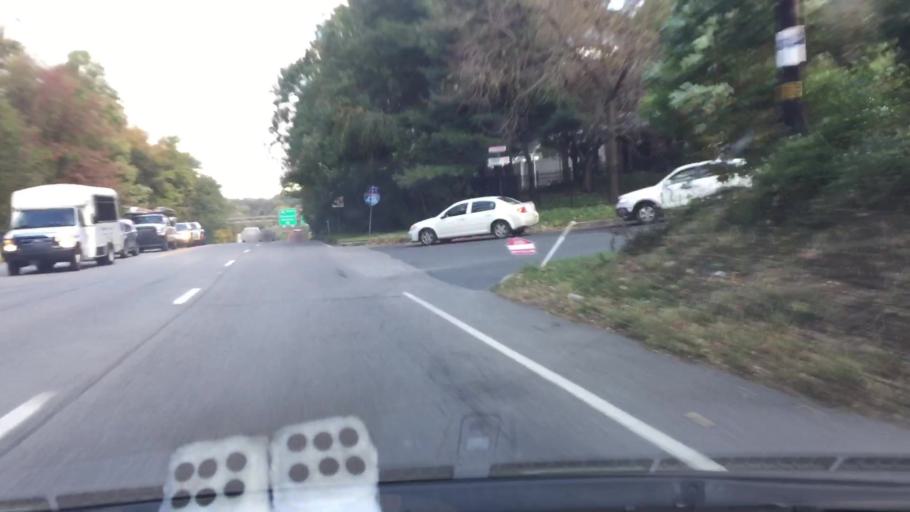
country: US
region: Pennsylvania
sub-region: Delaware County
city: Swarthmore
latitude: 39.9133
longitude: -75.3672
